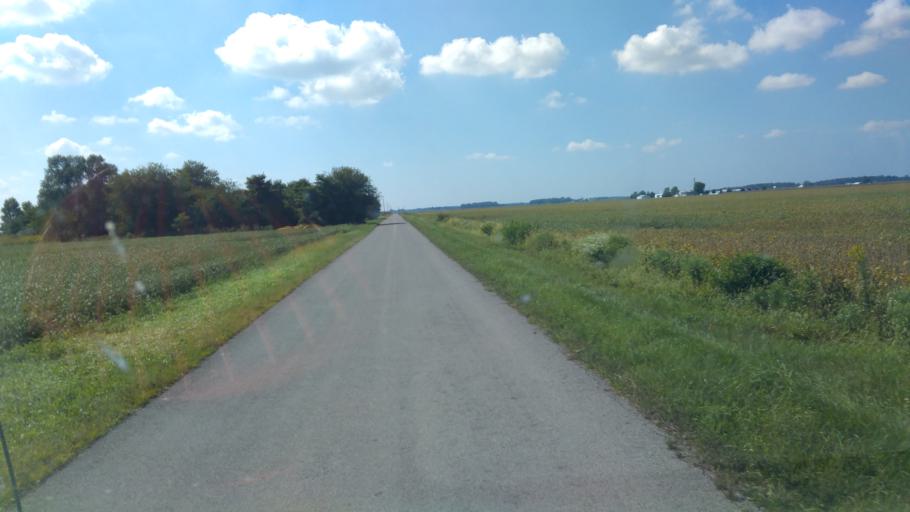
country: US
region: Ohio
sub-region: Logan County
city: Lakeview
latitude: 40.5868
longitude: -83.8696
